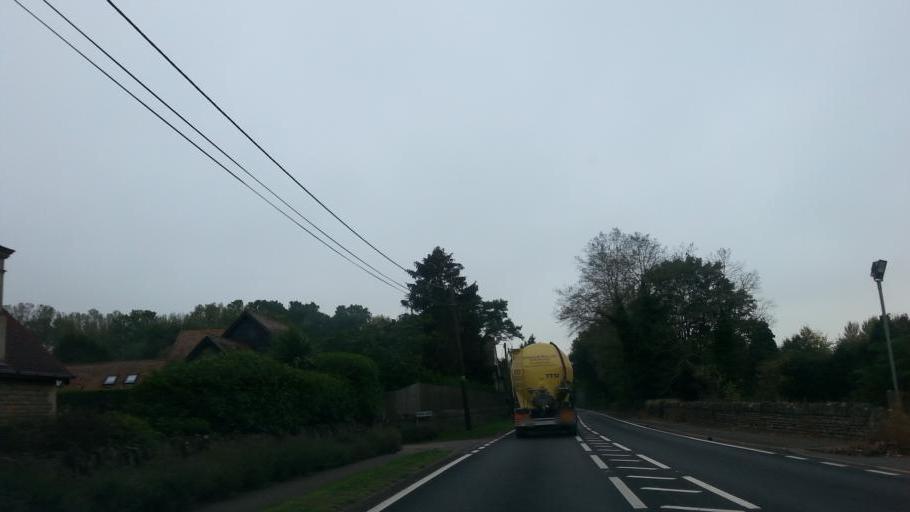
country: GB
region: England
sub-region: Northamptonshire
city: Thrapston
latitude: 52.4216
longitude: -0.4950
